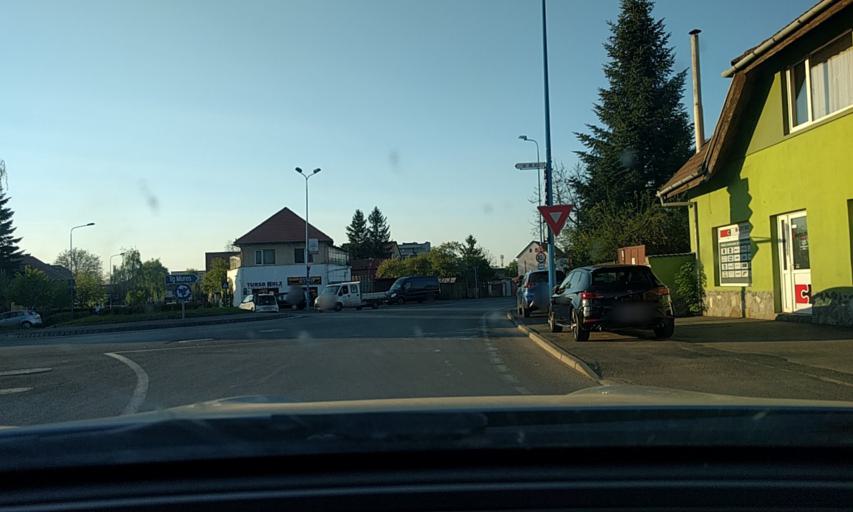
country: RO
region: Brasov
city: Brasov
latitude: 45.6664
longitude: 25.5777
